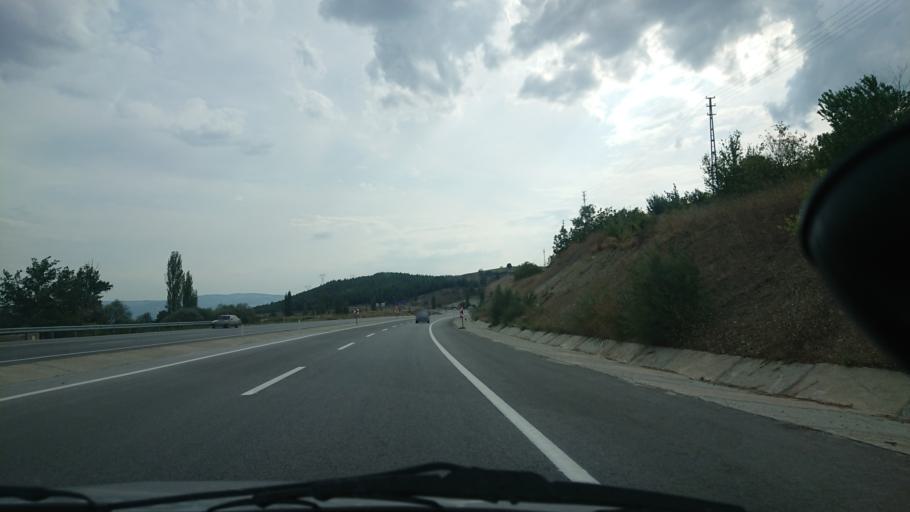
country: TR
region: Kuetahya
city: Gediz
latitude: 39.0361
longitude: 29.4202
